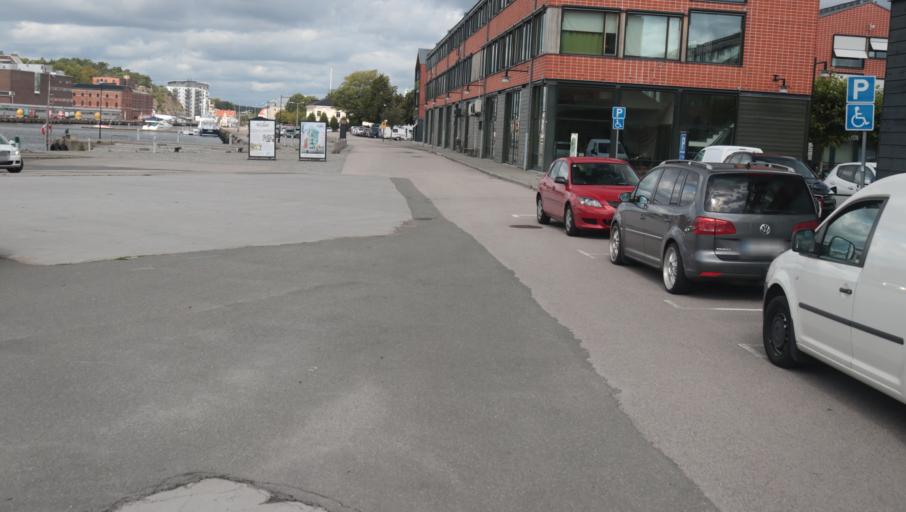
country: SE
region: Blekinge
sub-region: Karlshamns Kommun
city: Karlshamn
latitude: 56.1637
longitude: 14.8663
